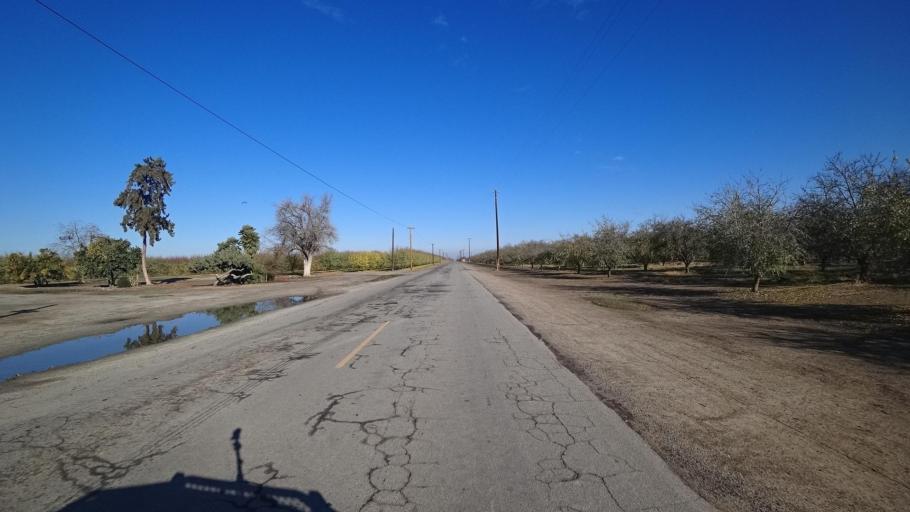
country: US
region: California
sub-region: Kern County
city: Delano
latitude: 35.7291
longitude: -119.3119
